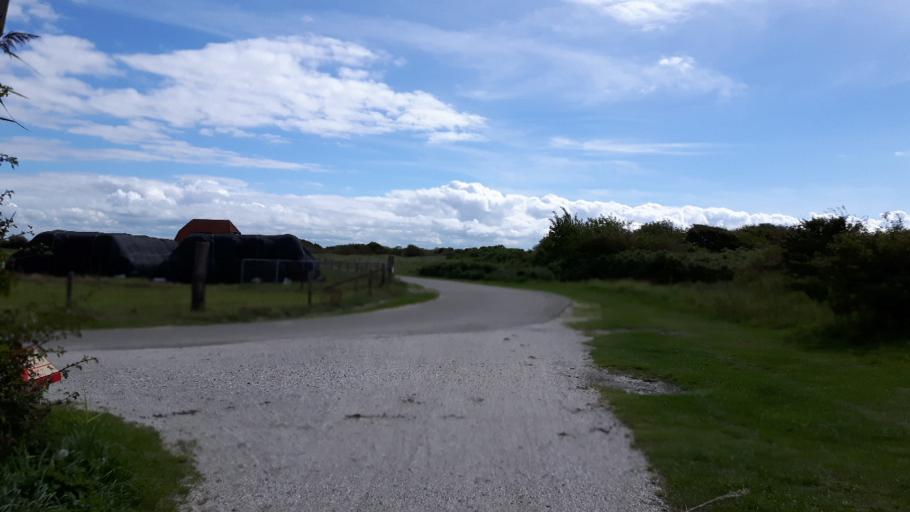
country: NL
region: Friesland
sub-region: Gemeente Ameland
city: Hollum
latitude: 53.4404
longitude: 5.6204
